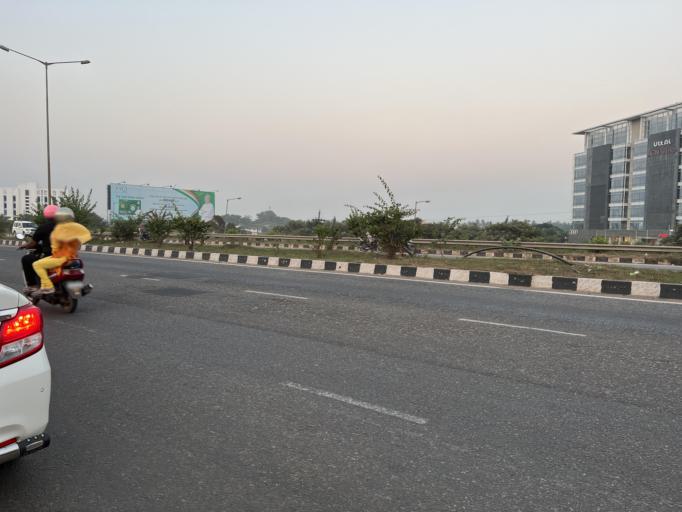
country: IN
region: Odisha
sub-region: Khordha
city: Bhubaneshwar
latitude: 20.3371
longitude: 85.8832
